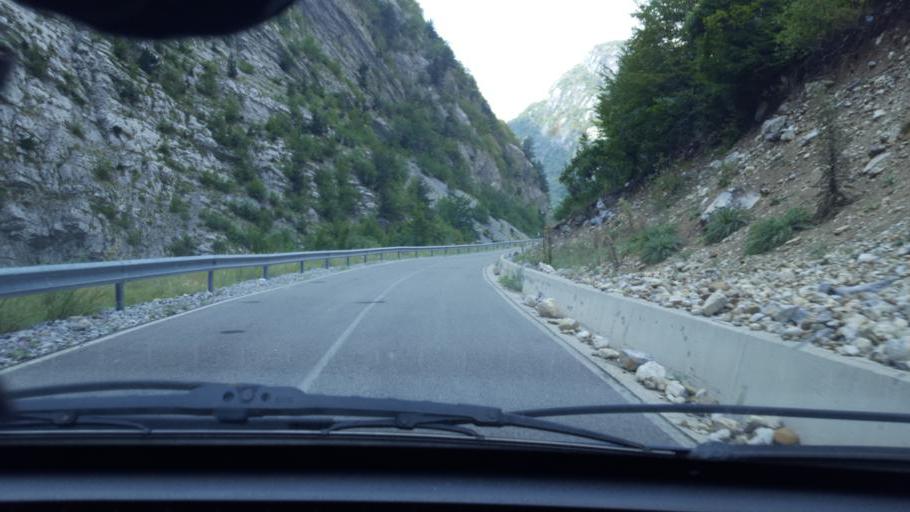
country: AL
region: Shkoder
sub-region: Rrethi i Malesia e Madhe
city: Kastrat
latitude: 42.5320
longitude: 19.6537
